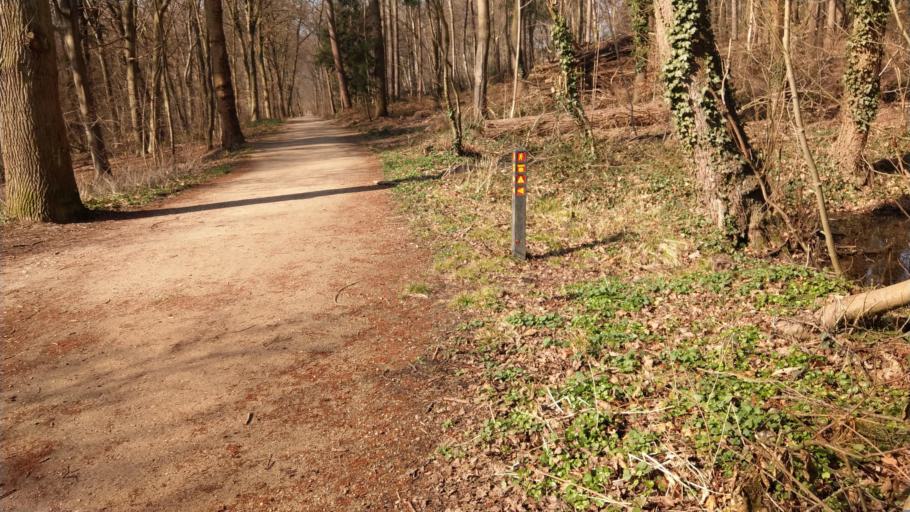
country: DE
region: North Rhine-Westphalia
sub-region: Regierungsbezirk Koln
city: Wassenberg
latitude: 51.1011
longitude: 6.1684
